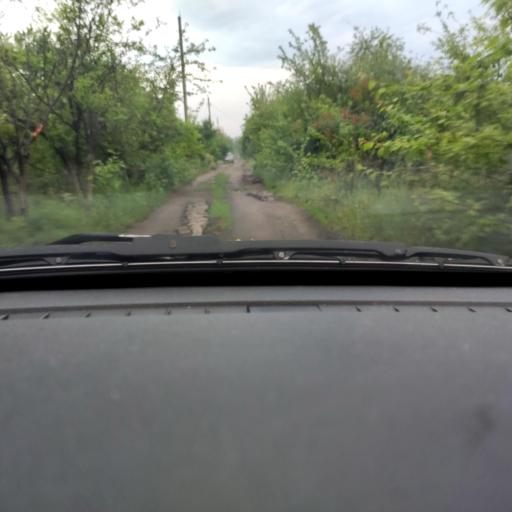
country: RU
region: Voronezj
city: Maslovka
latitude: 51.4930
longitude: 39.2138
